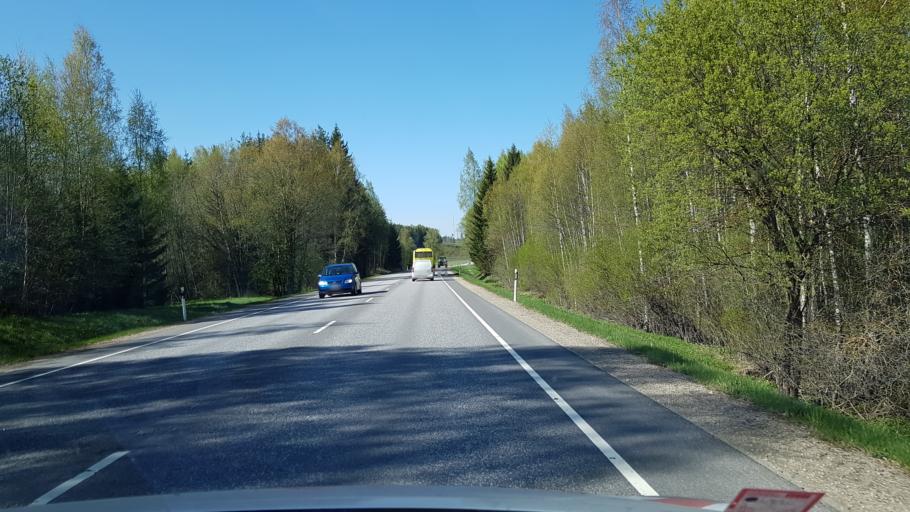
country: EE
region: Vorumaa
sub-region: Antsla vald
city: Vana-Antsla
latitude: 58.0294
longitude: 26.7359
